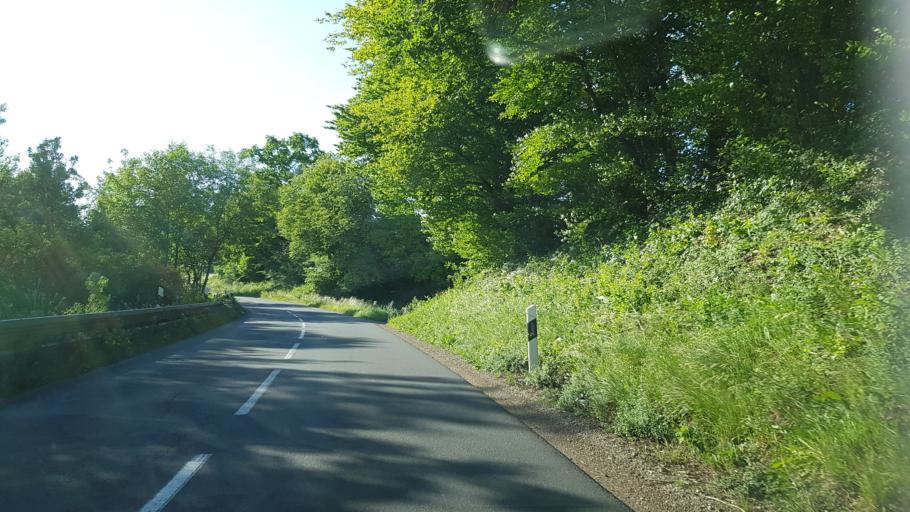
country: DE
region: Lower Saxony
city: Coppengrave
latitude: 51.9822
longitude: 9.7433
